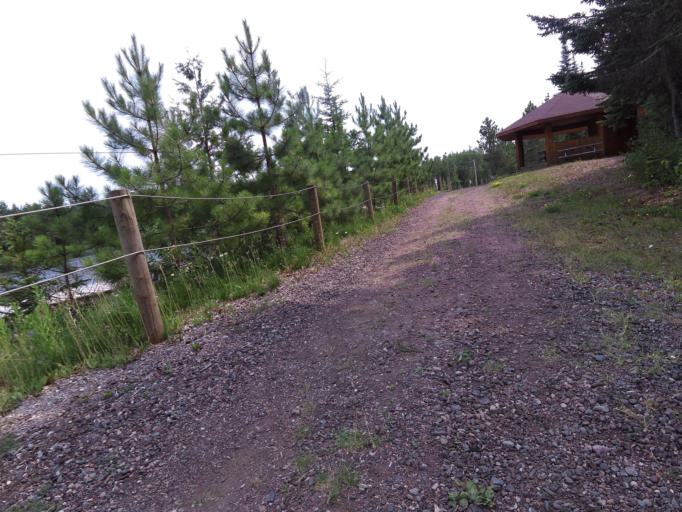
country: CA
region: Ontario
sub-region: Thunder Bay District
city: Thunder Bay
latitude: 48.7965
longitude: -88.6196
